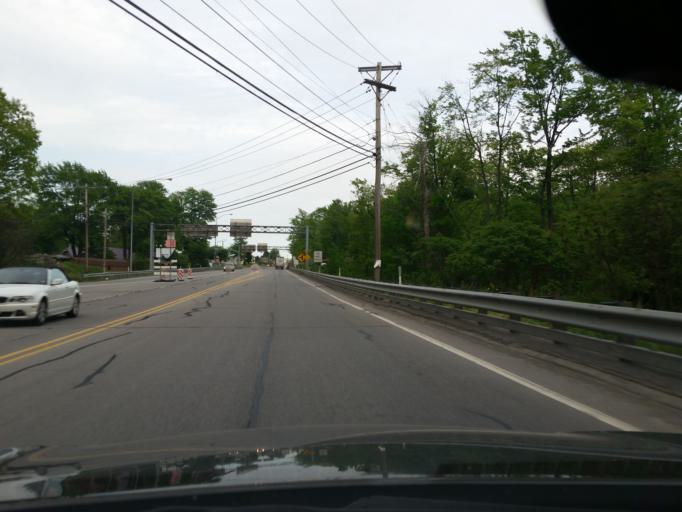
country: US
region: Pennsylvania
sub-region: Elk County
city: Ridgway
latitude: 41.4119
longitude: -78.7135
